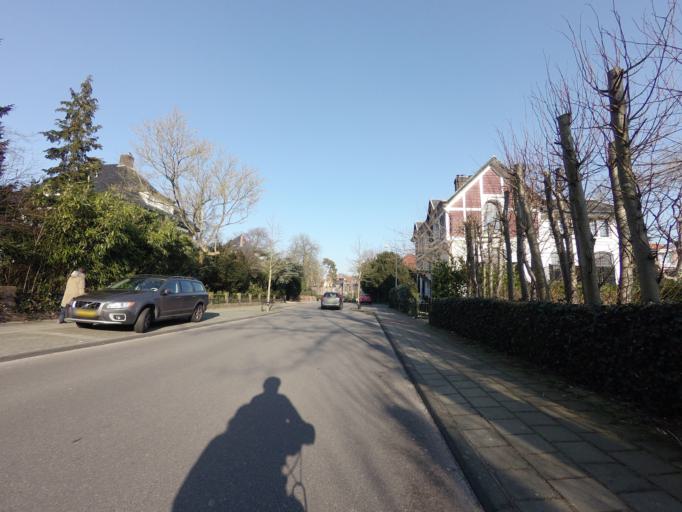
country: NL
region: North Holland
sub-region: Gemeente Bloemendaal
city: Bloemendaal
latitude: 52.3998
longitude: 4.6151
